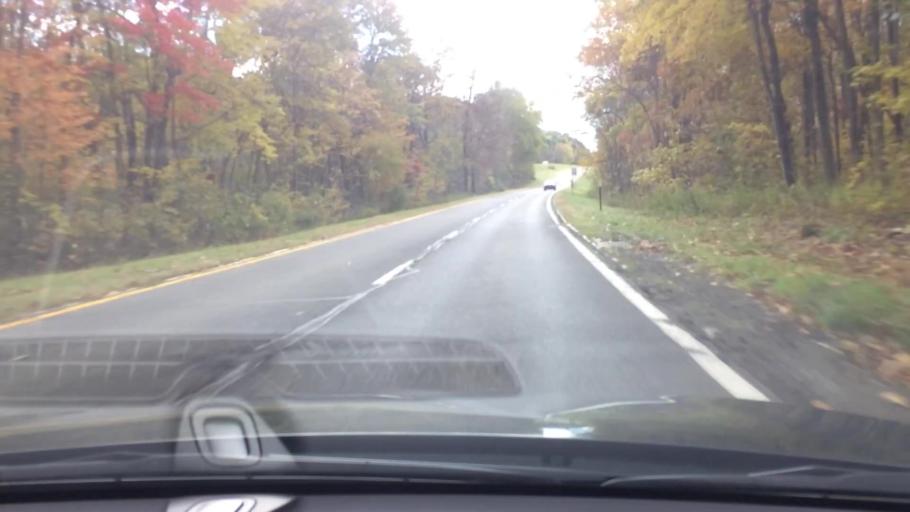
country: US
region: New York
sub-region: Dutchess County
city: Pine Plains
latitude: 41.9481
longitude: -73.7524
